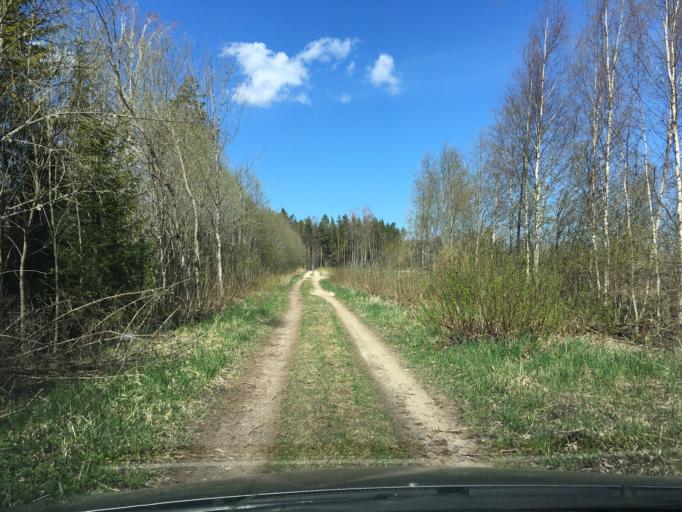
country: EE
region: Harju
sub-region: Raasiku vald
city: Arukula
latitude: 59.2080
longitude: 25.1195
